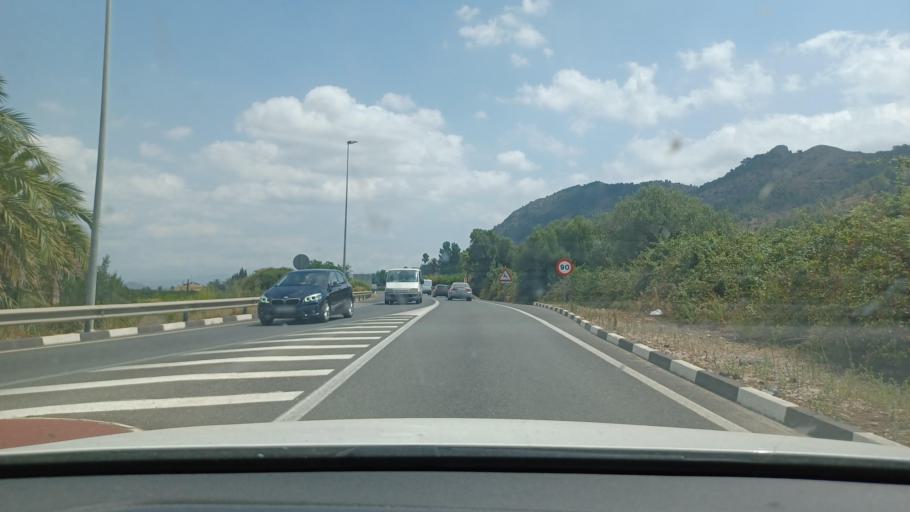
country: ES
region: Valencia
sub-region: Provincia de Valencia
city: Cerda
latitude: 38.9716
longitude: -0.5613
